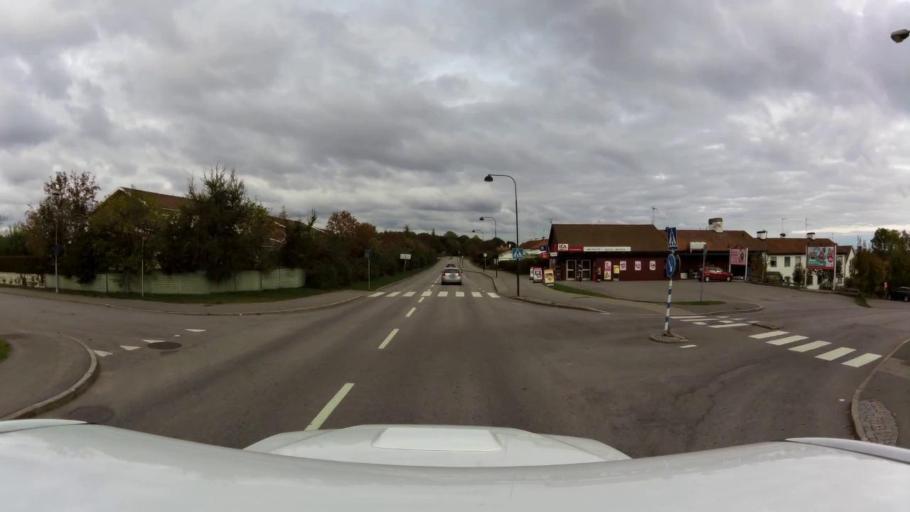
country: SE
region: OEstergoetland
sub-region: Linkopings Kommun
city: Berg
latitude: 58.4888
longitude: 15.5257
